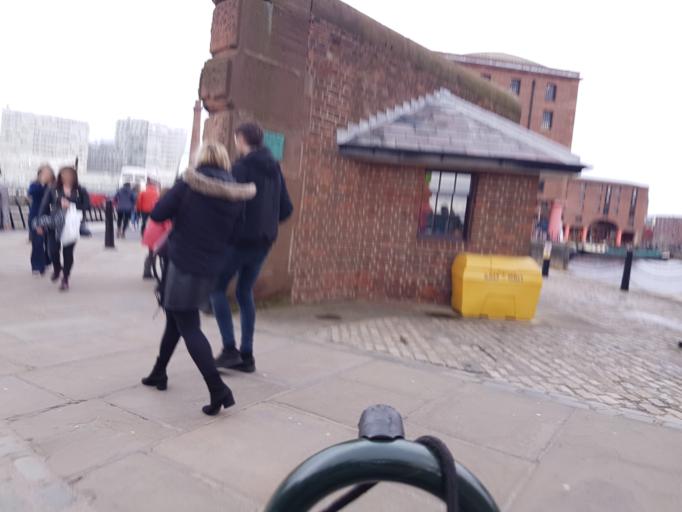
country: GB
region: England
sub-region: Liverpool
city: Liverpool
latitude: 53.4012
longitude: -2.9943
